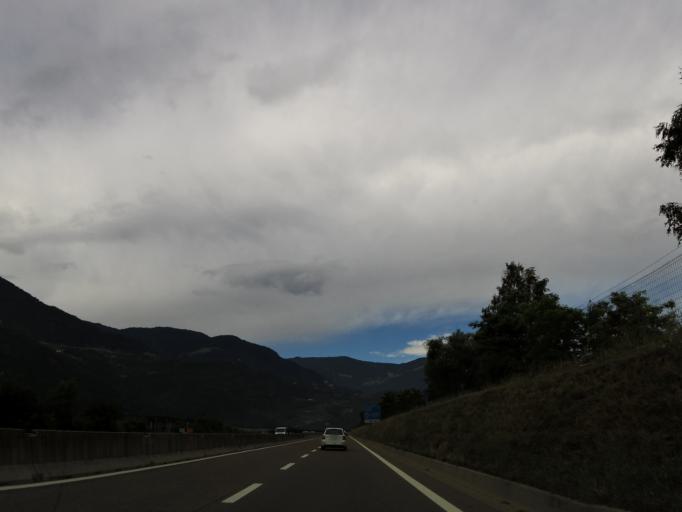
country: IT
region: Trentino-Alto Adige
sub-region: Bolzano
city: Gargazzone
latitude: 46.5697
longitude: 11.2063
